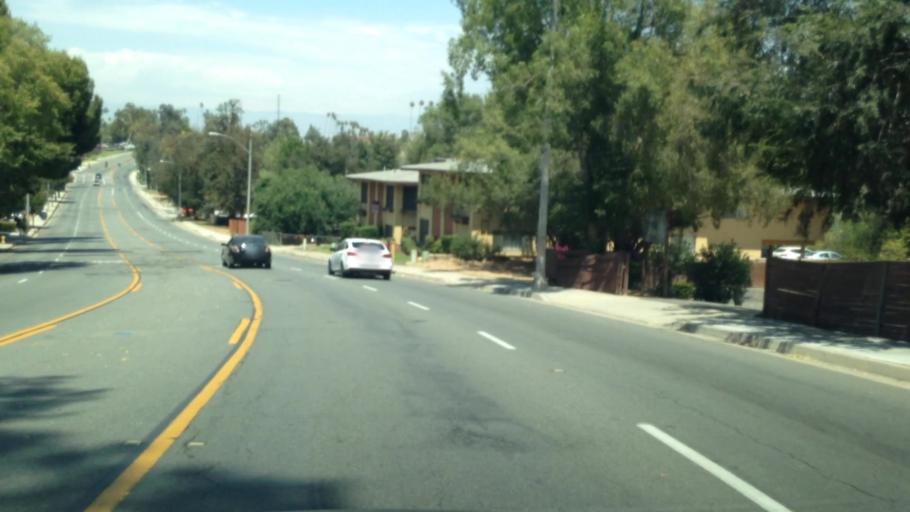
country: US
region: California
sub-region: Riverside County
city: Riverside
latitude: 33.9652
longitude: -117.3802
